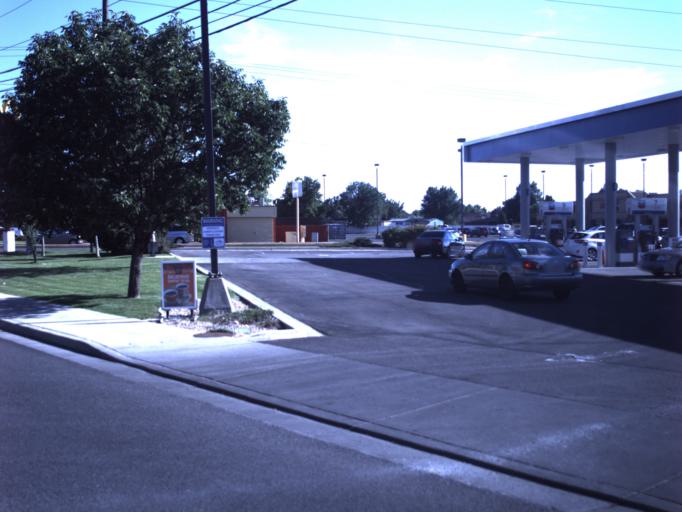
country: US
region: Utah
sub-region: Utah County
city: Lindon
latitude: 40.3272
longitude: -111.7084
